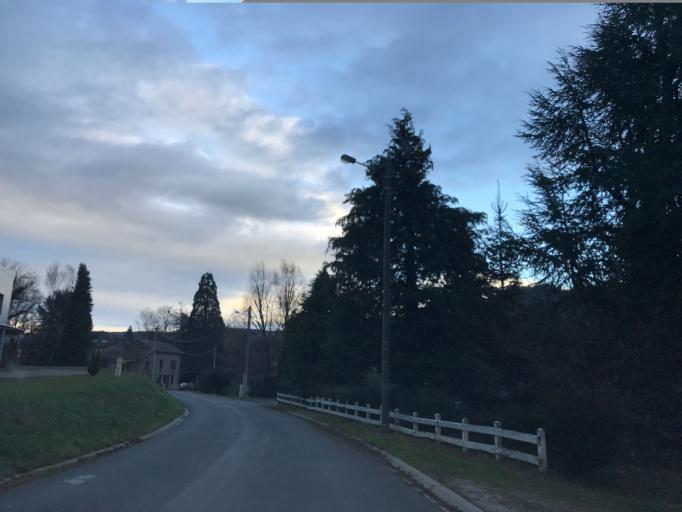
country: FR
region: Auvergne
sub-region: Departement du Puy-de-Dome
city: Celles-sur-Durolle
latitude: 45.8273
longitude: 3.6709
